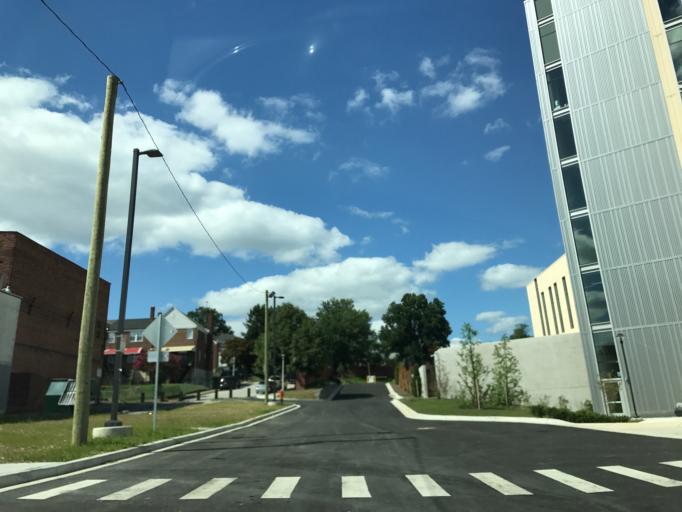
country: US
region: Maryland
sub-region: City of Baltimore
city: Baltimore
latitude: 39.3409
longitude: -76.5895
